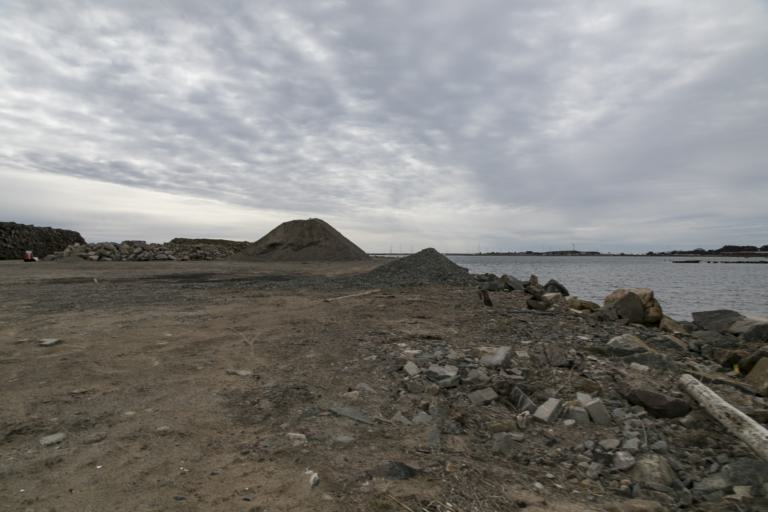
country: SE
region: Halland
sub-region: Varbergs Kommun
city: Varberg
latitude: 57.1194
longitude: 12.2351
